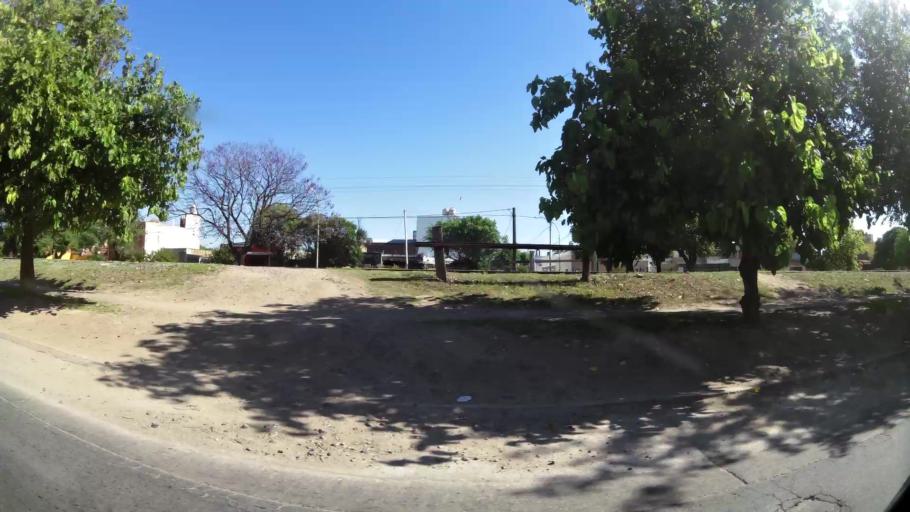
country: AR
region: Cordoba
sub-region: Departamento de Capital
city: Cordoba
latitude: -31.4405
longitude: -64.1659
